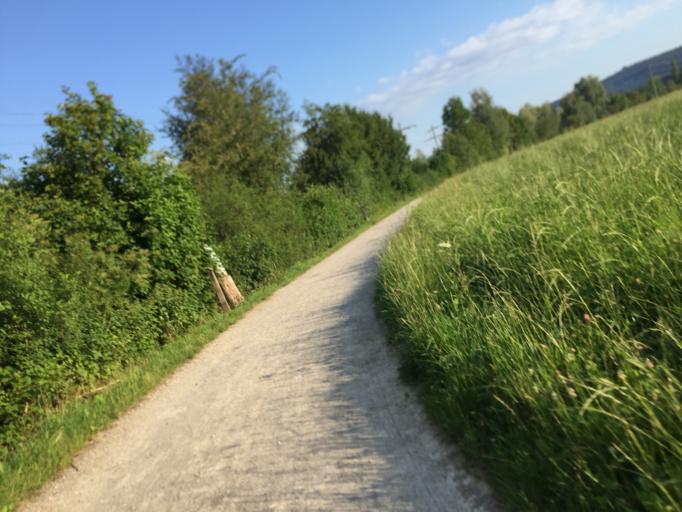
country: CH
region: Bern
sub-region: Bern-Mittelland District
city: Rubigen
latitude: 46.9111
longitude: 7.5392
